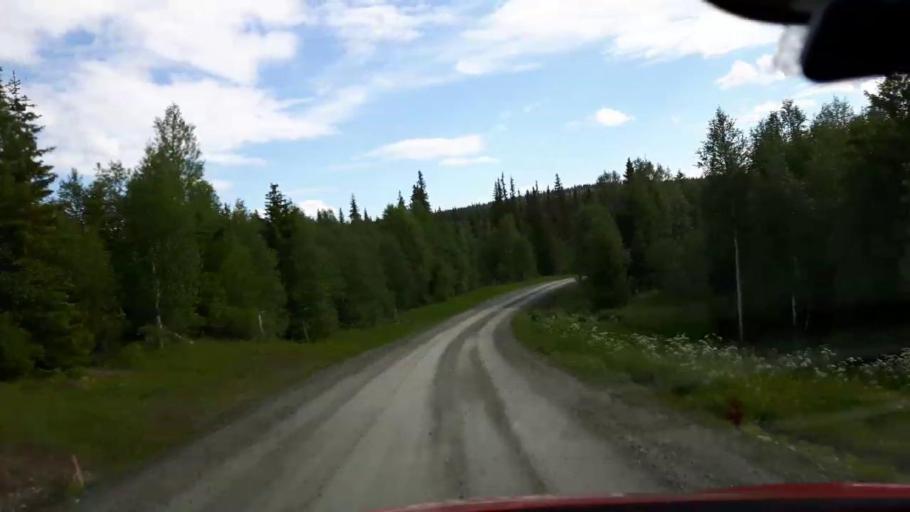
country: SE
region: Jaemtland
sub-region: Krokoms Kommun
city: Valla
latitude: 63.8831
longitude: 14.1486
